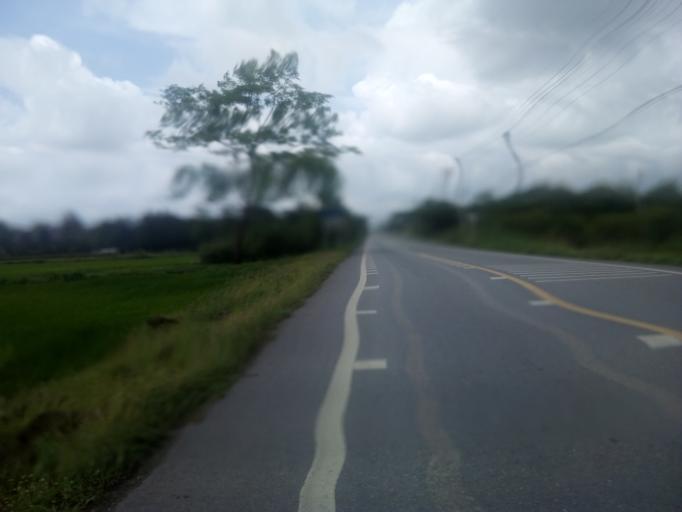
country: TH
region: Pathum Thani
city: Ban Lam Luk Ka
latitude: 14.0128
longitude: 100.8230
